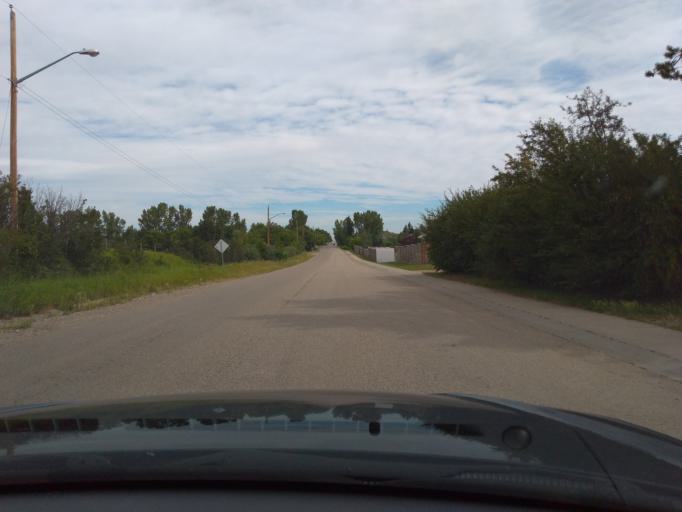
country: CA
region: Alberta
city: Didsbury
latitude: 51.6511
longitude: -114.1433
